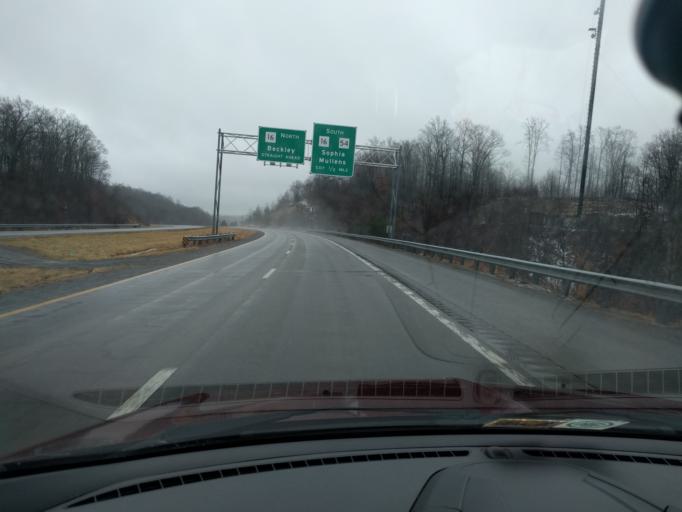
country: US
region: West Virginia
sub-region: Raleigh County
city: Sophia
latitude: 37.7127
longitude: -81.2653
